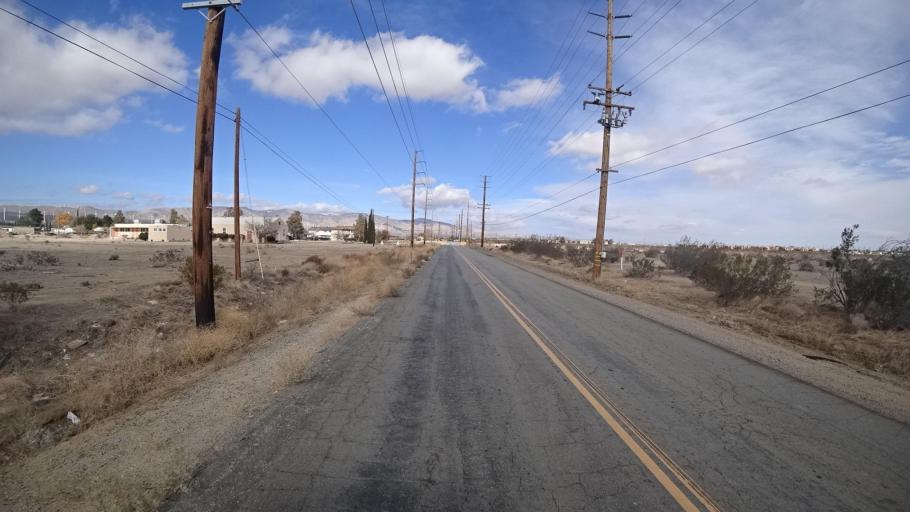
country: US
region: California
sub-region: Kern County
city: Mojave
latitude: 35.0489
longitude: -118.1855
